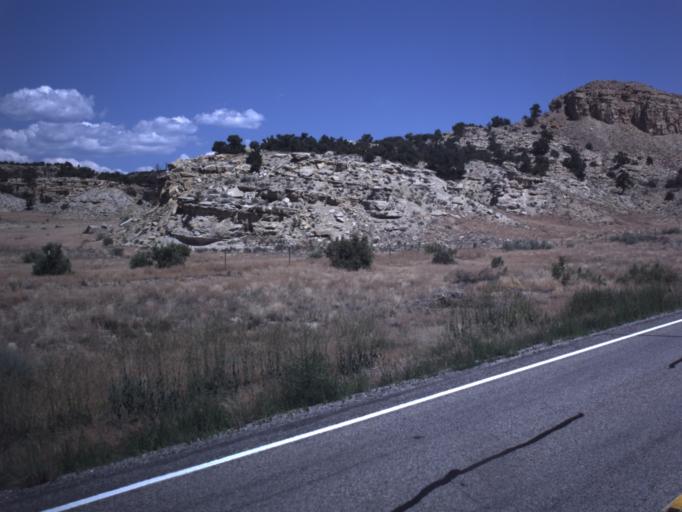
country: US
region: Utah
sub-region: Emery County
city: Ferron
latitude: 38.8224
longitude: -111.3270
